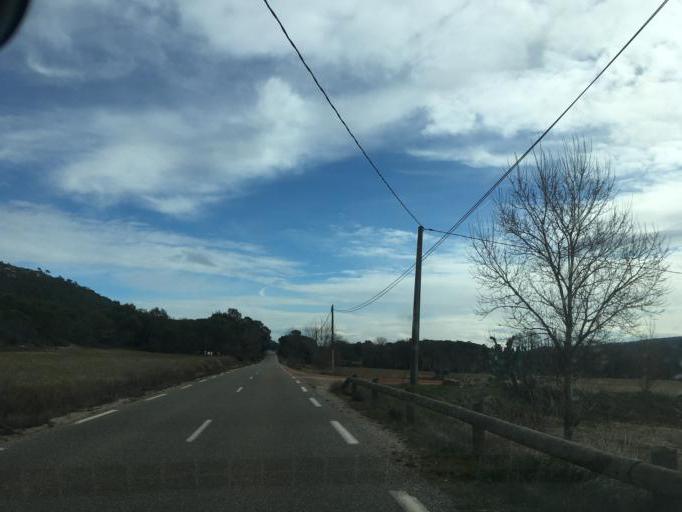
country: FR
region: Provence-Alpes-Cote d'Azur
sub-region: Departement du Var
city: La Celle
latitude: 43.4457
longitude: 6.0090
